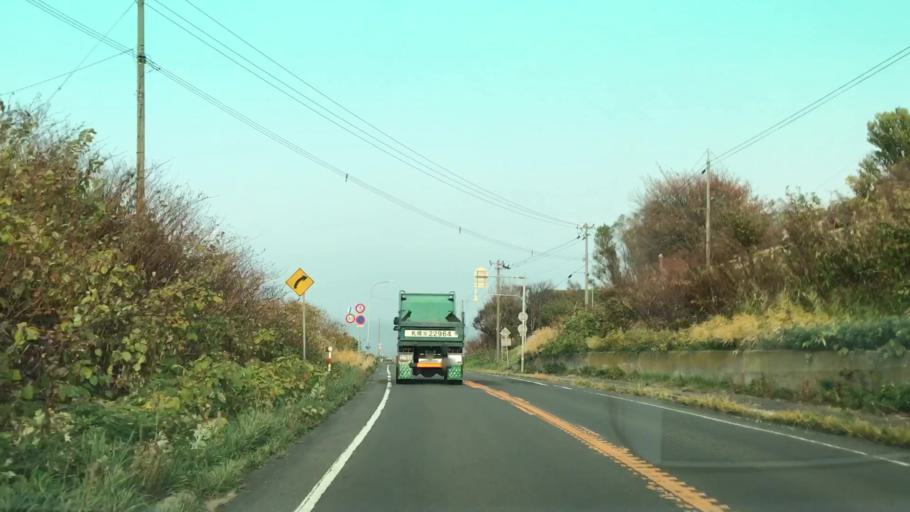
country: JP
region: Hokkaido
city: Ishikari
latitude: 43.4229
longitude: 141.4276
